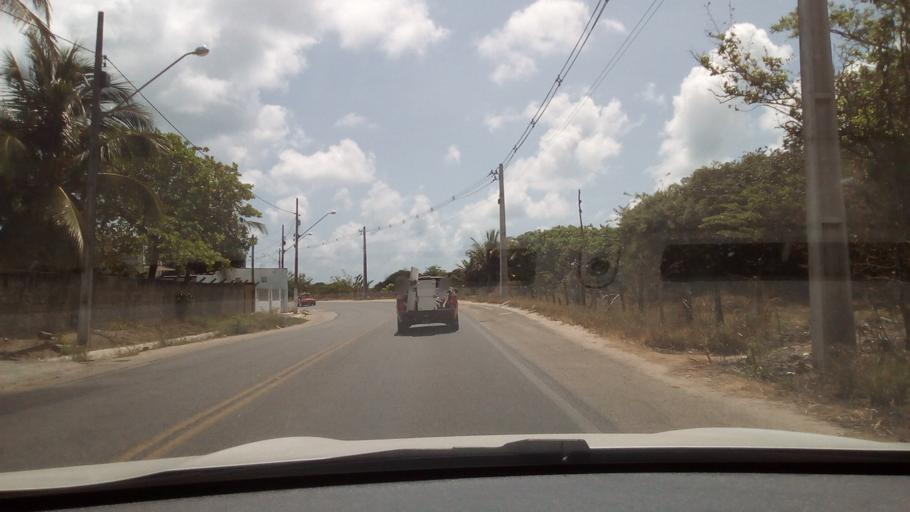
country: BR
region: Paraiba
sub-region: Joao Pessoa
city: Joao Pessoa
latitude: -7.1979
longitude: -34.8168
